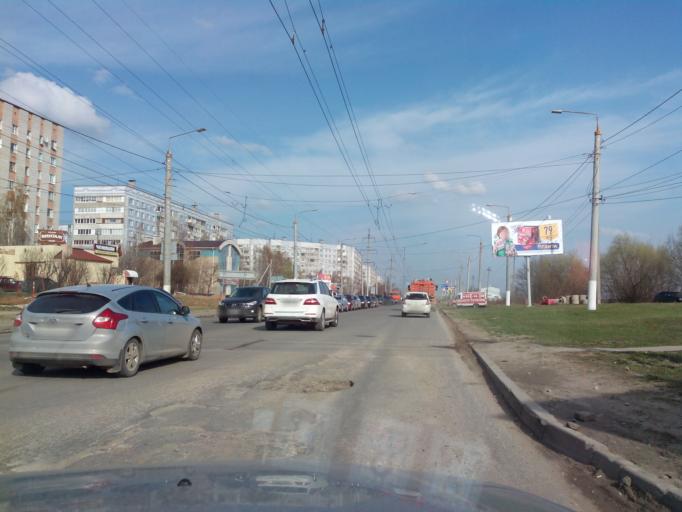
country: RU
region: Rjazan
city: Ryazan'
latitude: 54.6601
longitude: 39.6640
